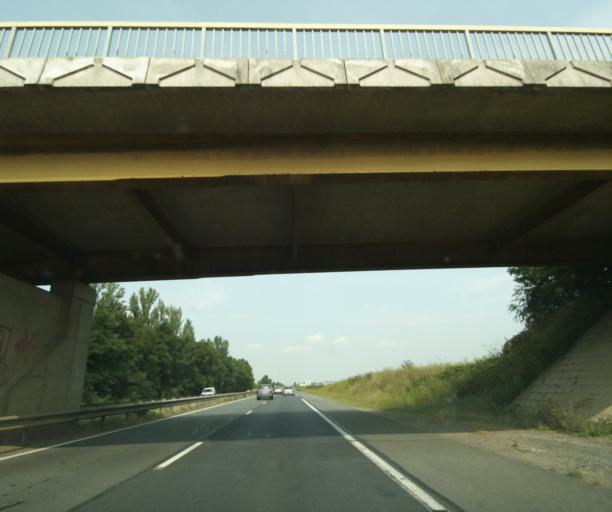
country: FR
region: Lower Normandy
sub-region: Departement du Calvados
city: Bretteville-sur-Laize
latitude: 49.0554
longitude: -0.2869
